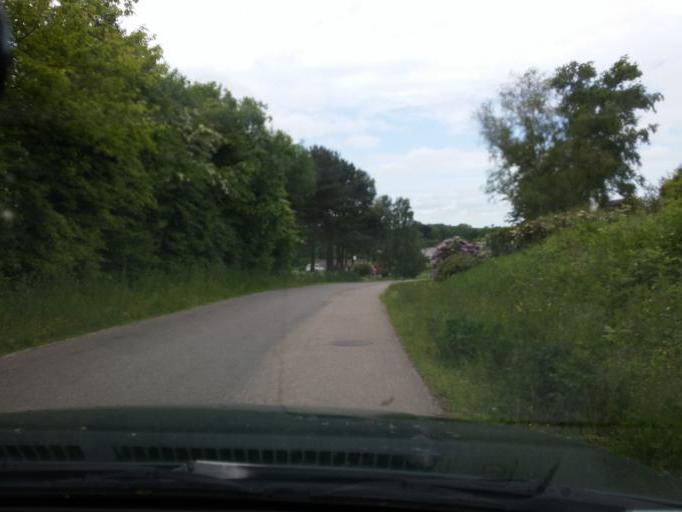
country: DK
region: South Denmark
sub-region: Aabenraa Kommune
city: Lojt Kirkeby
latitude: 55.1355
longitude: 9.4939
